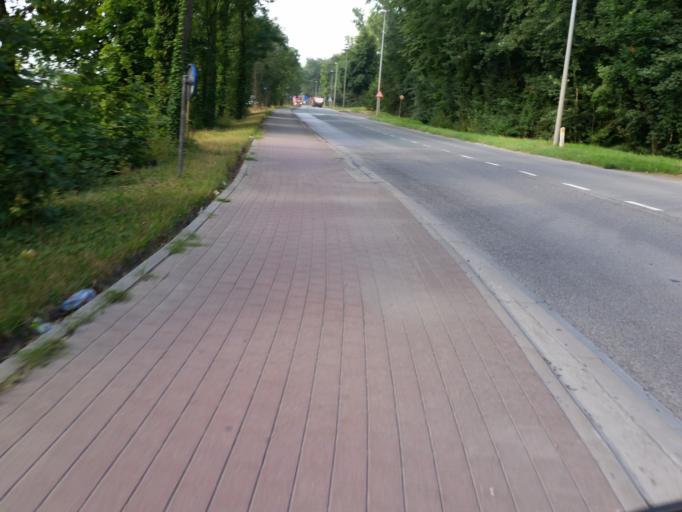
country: BE
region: Flanders
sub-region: Provincie Vlaams-Brabant
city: Vilvoorde
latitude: 50.9149
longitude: 4.4158
